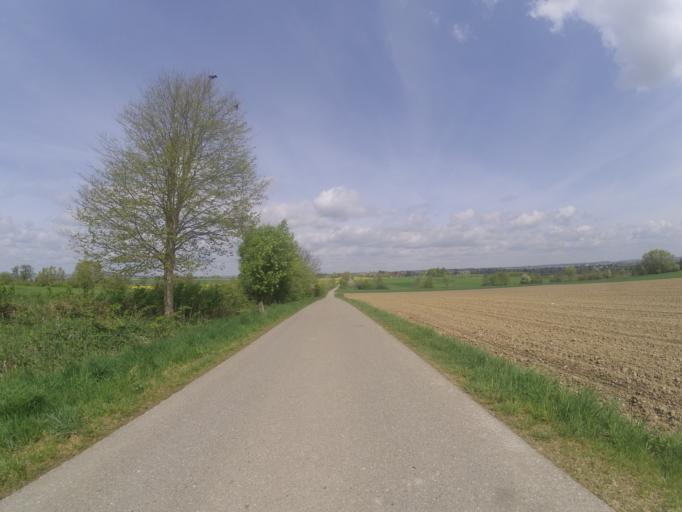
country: DE
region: Baden-Wuerttemberg
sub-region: Tuebingen Region
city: Griesingen
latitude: 48.2545
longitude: 9.7760
